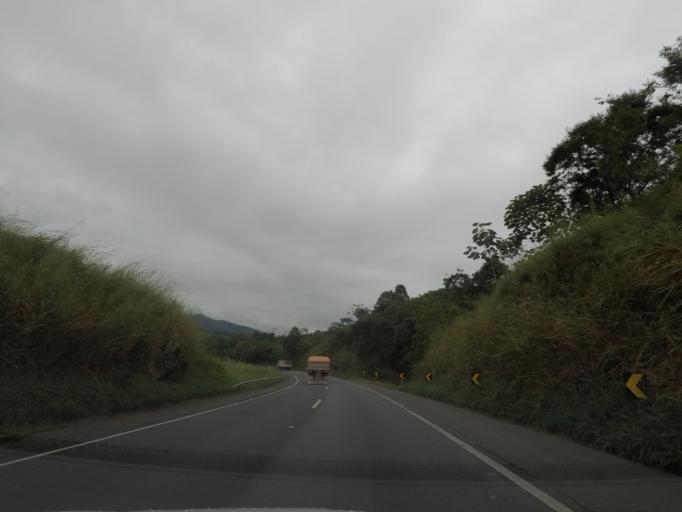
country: BR
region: Sao Paulo
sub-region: Cajati
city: Cajati
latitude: -24.8230
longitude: -48.2091
